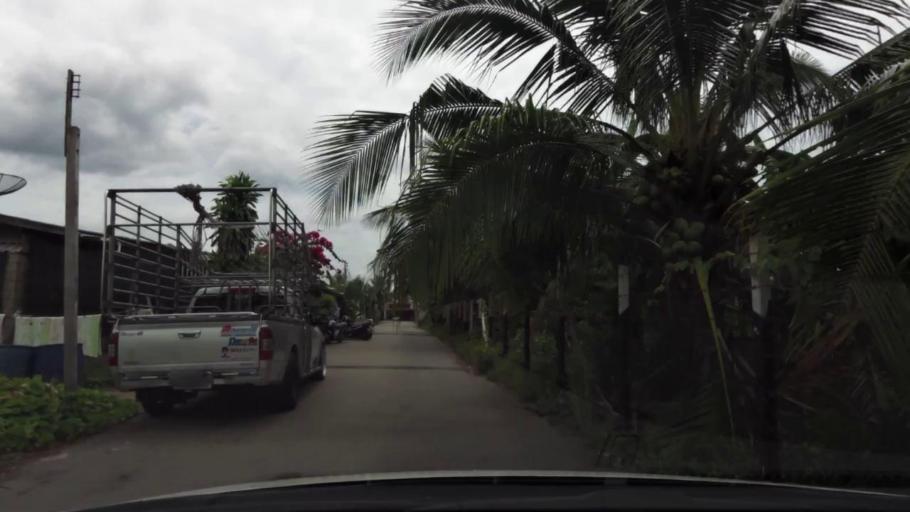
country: TH
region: Samut Sakhon
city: Ban Phaeo
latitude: 13.5672
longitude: 100.0337
